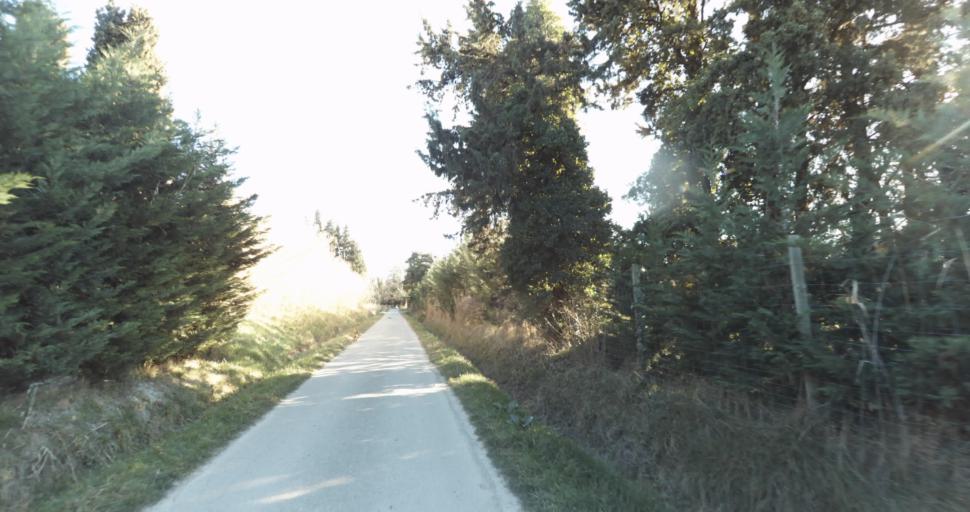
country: FR
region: Provence-Alpes-Cote d'Azur
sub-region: Departement des Bouches-du-Rhone
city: Barbentane
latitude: 43.9164
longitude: 4.7468
